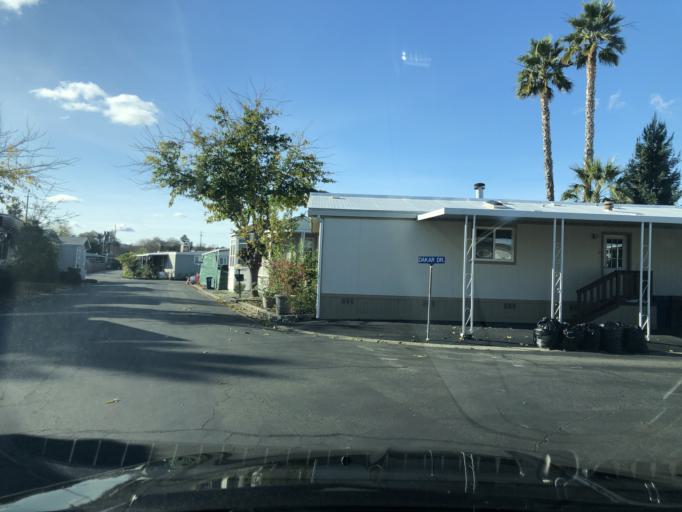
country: US
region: California
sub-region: Contra Costa County
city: Pacheco
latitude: 37.9858
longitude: -122.0639
